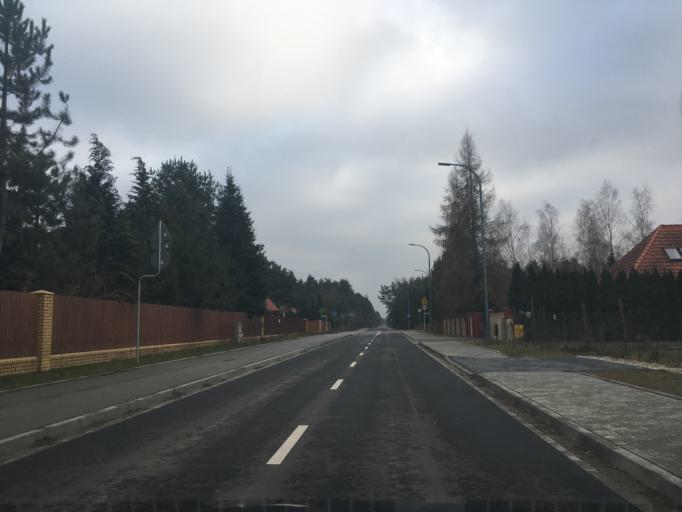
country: PL
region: Masovian Voivodeship
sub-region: Powiat piaseczynski
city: Lesznowola
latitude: 52.0684
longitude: 20.9717
